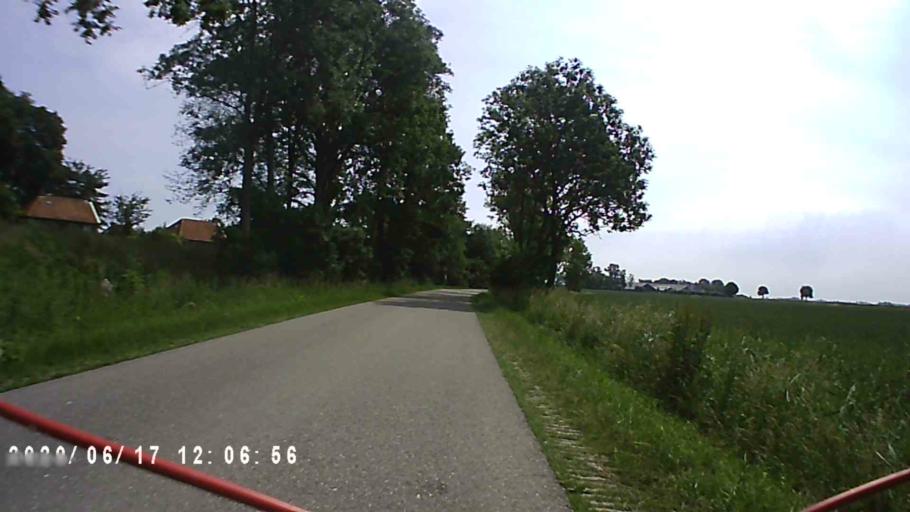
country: NL
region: Groningen
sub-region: Gemeente De Marne
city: Ulrum
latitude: 53.3355
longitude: 6.3605
